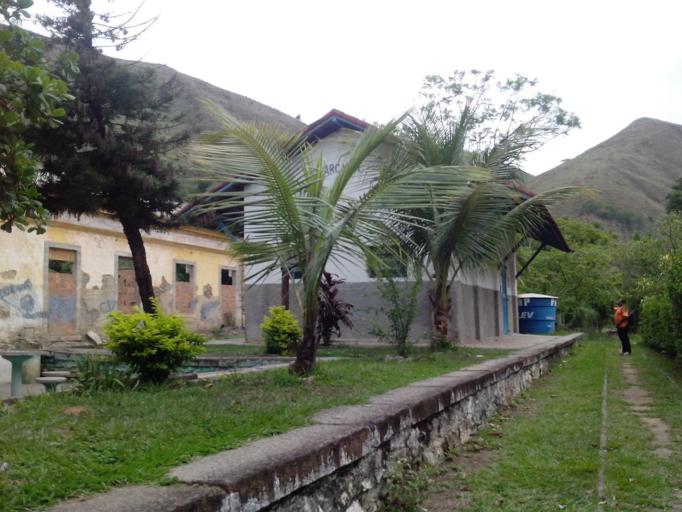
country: BR
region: Rio de Janeiro
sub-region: Miguel Pereira
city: Miguel Pereira
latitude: -22.5099
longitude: -43.5236
